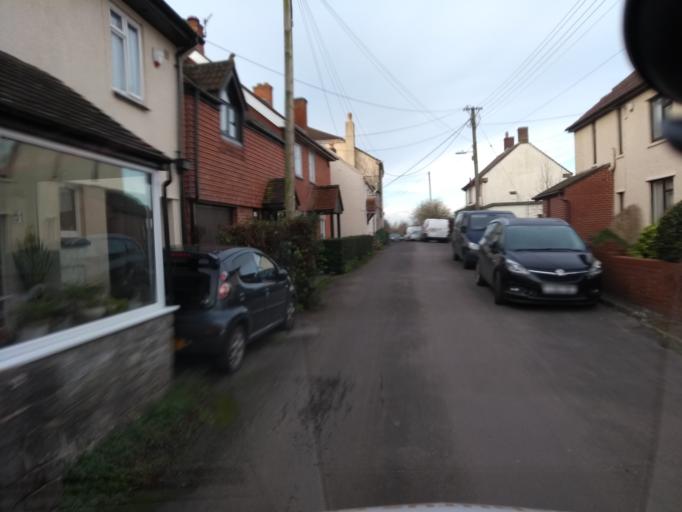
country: GB
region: England
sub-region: Somerset
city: Glastonbury
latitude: 51.1425
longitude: -2.7204
